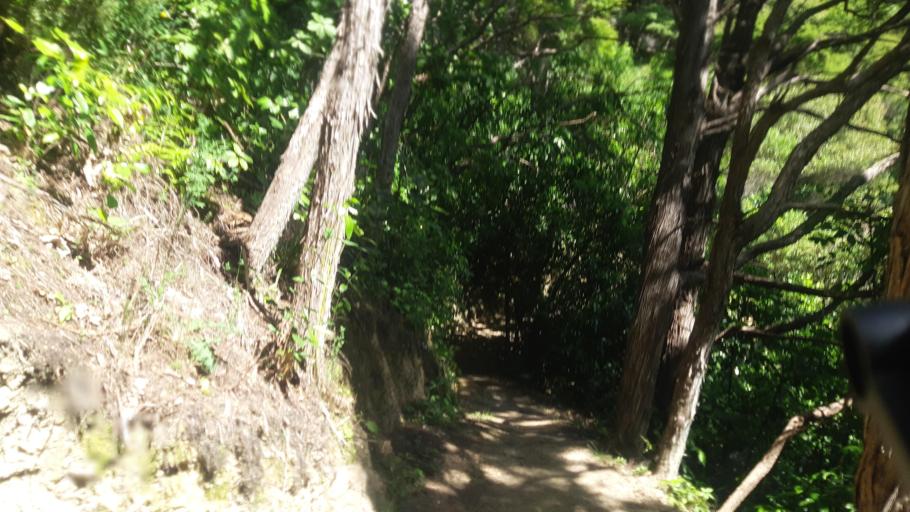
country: NZ
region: Marlborough
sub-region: Marlborough District
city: Picton
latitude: -41.2579
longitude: 174.0358
